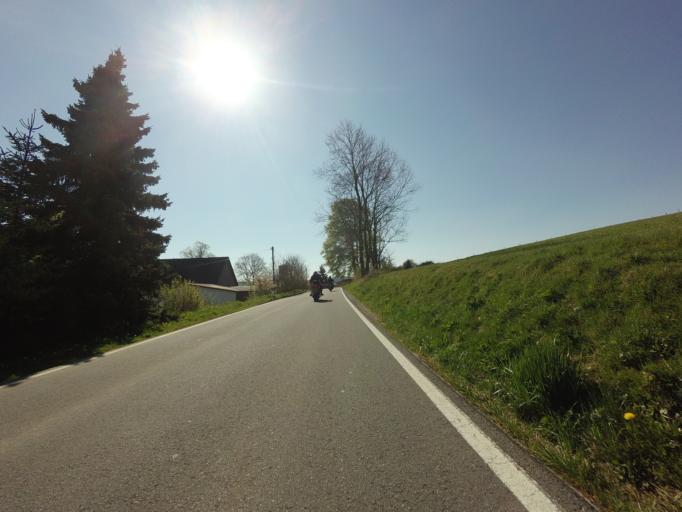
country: DE
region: North Rhine-Westphalia
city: Meinerzhagen
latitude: 51.1539
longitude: 7.6753
